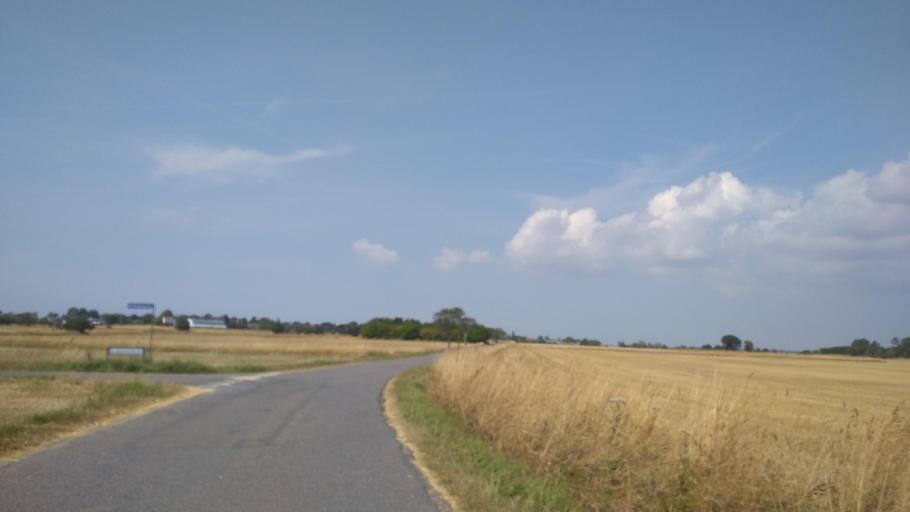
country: DK
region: Capital Region
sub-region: Bornholm Kommune
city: Akirkeby
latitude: 55.0633
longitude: 14.9385
